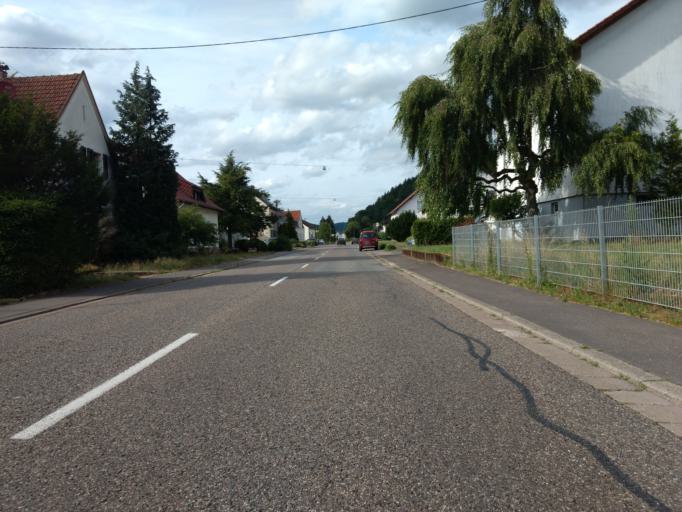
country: DE
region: Saarland
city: Beckingen
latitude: 49.4194
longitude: 6.7282
